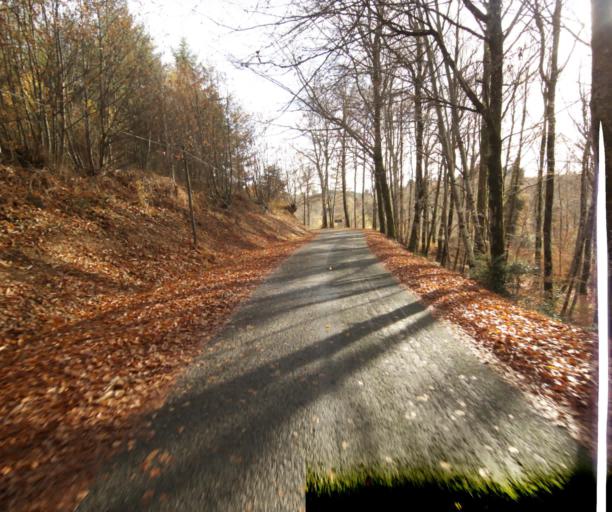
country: FR
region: Limousin
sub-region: Departement de la Correze
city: Sainte-Fortunade
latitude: 45.1976
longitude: 1.7340
